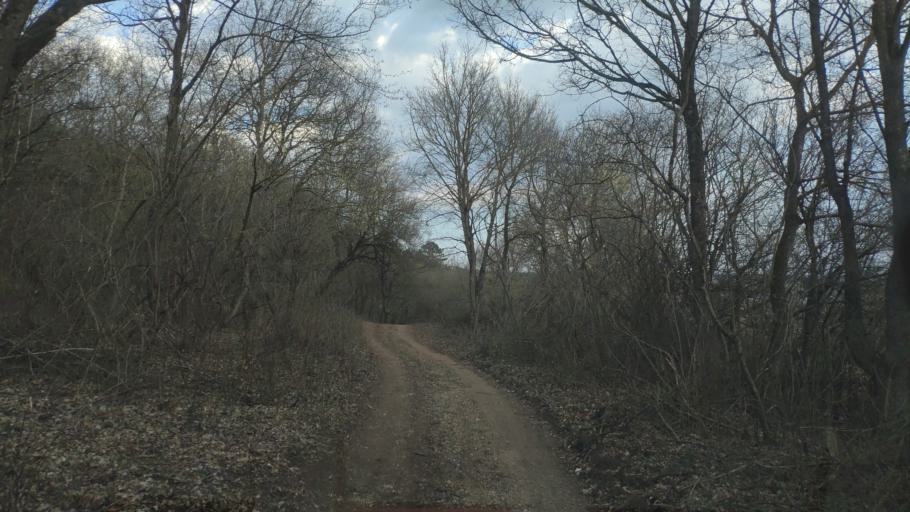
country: SK
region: Kosicky
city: Moldava nad Bodvou
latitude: 48.6200
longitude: 20.9266
